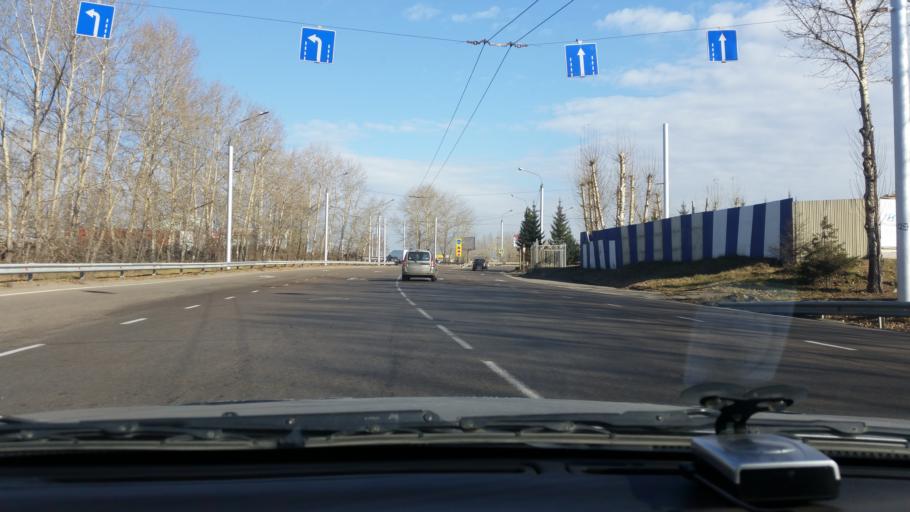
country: RU
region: Irkutsk
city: Dzerzhinsk
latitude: 52.2604
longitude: 104.3513
